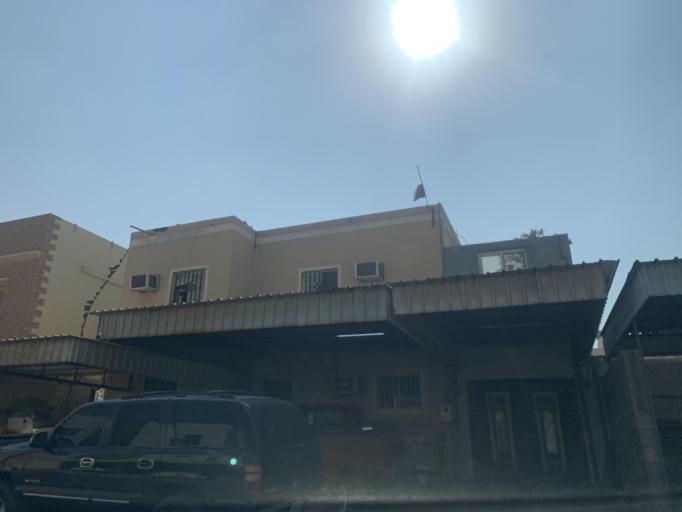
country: BH
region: Central Governorate
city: Madinat Hamad
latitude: 26.1281
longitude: 50.4936
